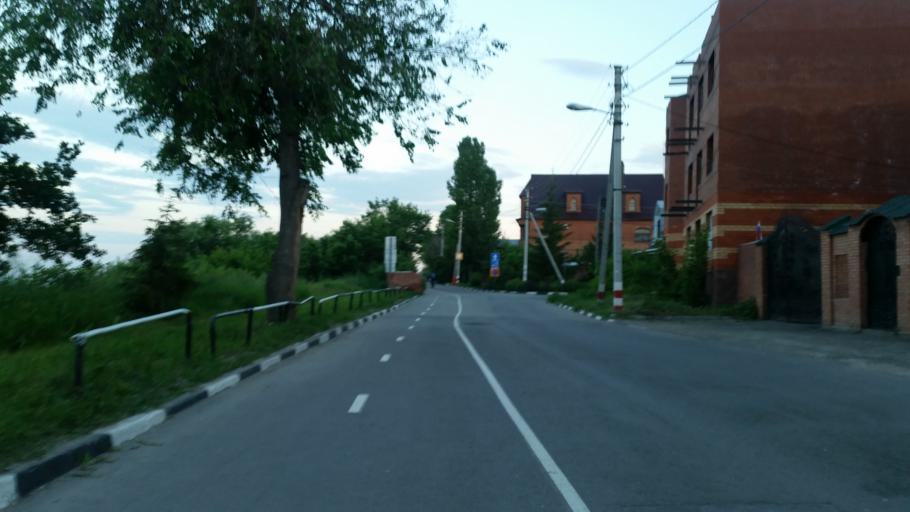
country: RU
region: Ulyanovsk
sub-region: Ulyanovskiy Rayon
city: Ulyanovsk
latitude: 54.3249
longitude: 48.4094
